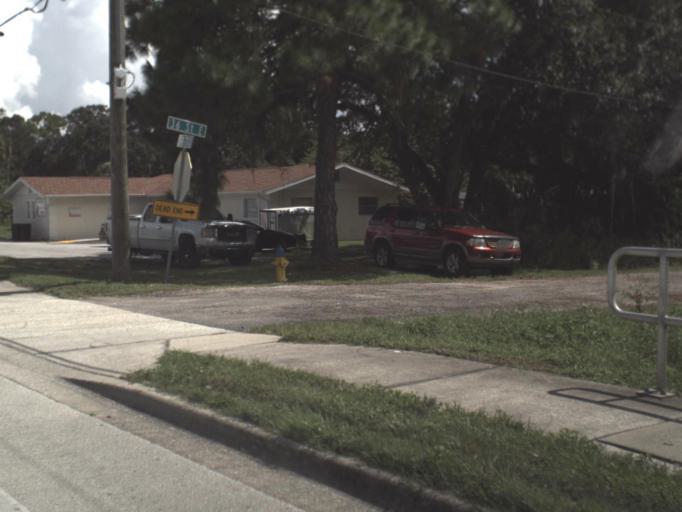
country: US
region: Florida
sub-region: Manatee County
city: Samoset
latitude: 27.4472
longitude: -82.5179
